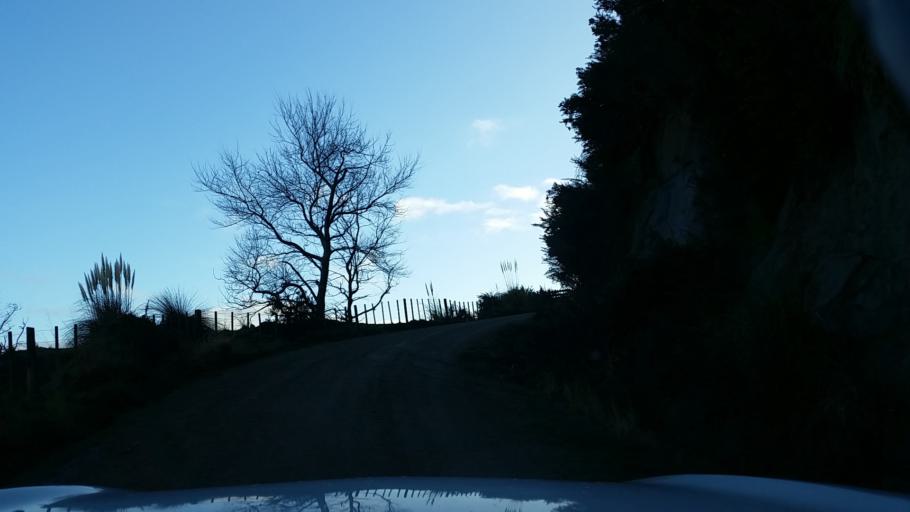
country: NZ
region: Taranaki
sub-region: South Taranaki District
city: Patea
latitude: -39.7583
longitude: 174.7387
